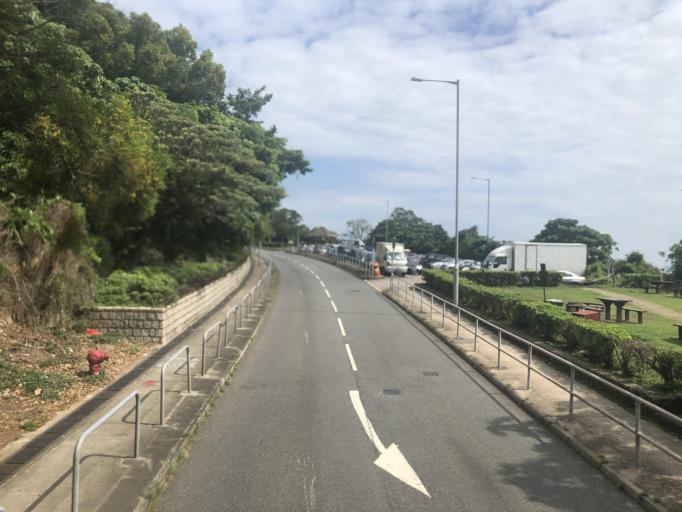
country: HK
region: Sai Kung
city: Sai Kung
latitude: 22.3922
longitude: 114.2896
